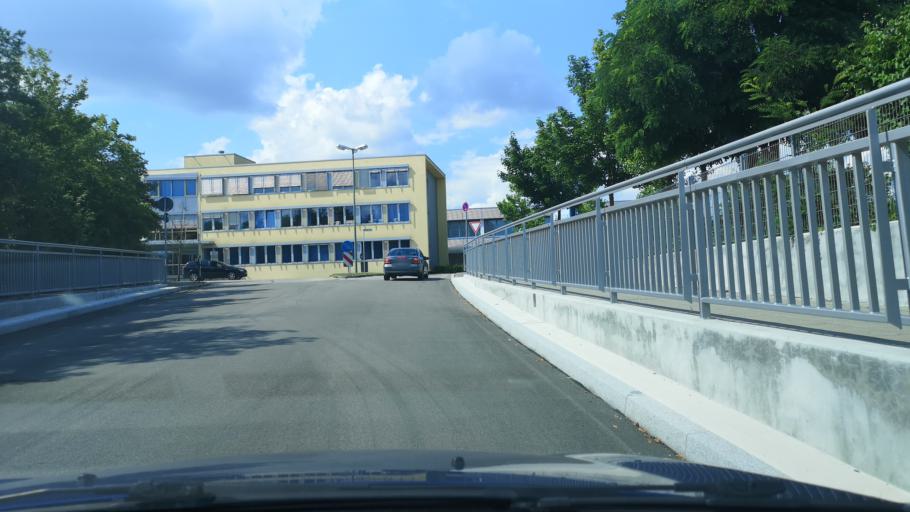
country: DE
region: Bavaria
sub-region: Upper Bavaria
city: Poing
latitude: 48.1695
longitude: 11.8012
